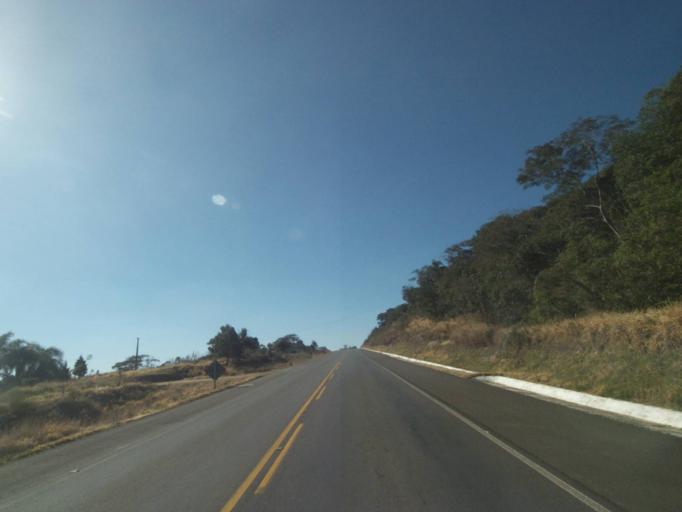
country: BR
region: Parana
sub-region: Tibagi
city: Tibagi
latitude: -24.7850
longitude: -50.4692
